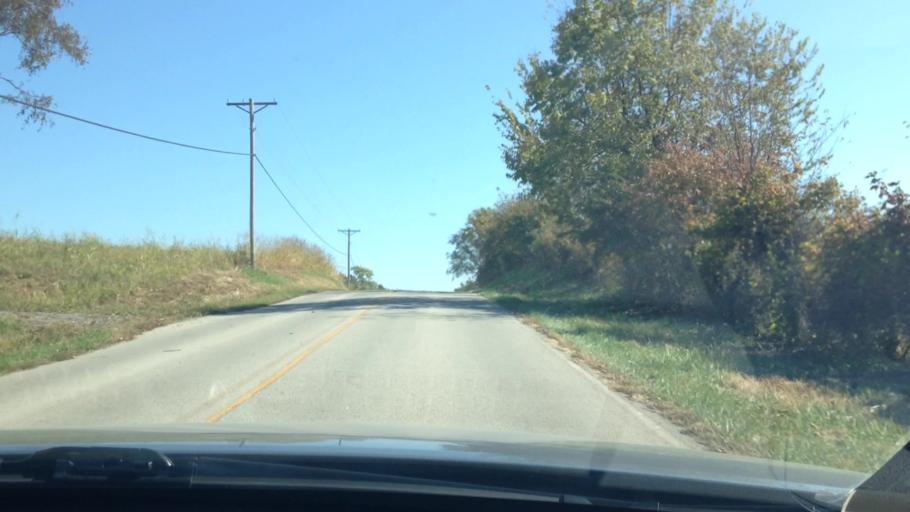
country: US
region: Missouri
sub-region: Platte County
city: Platte City
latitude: 39.3319
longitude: -94.8379
